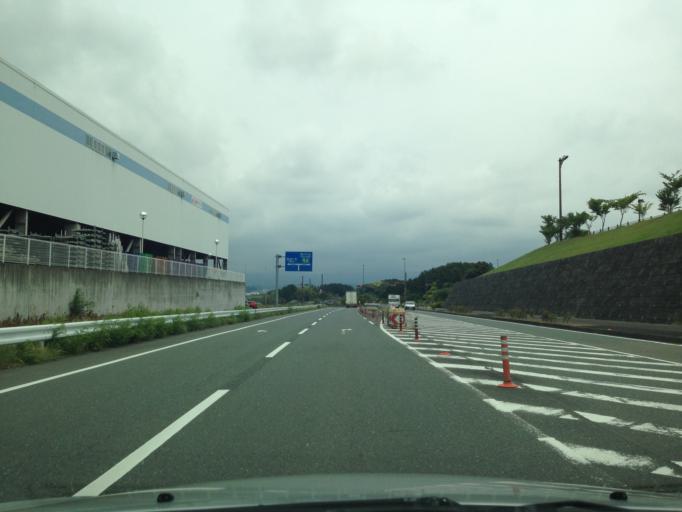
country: JP
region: Shizuoka
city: Kakegawa
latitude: 34.7503
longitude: 137.9736
